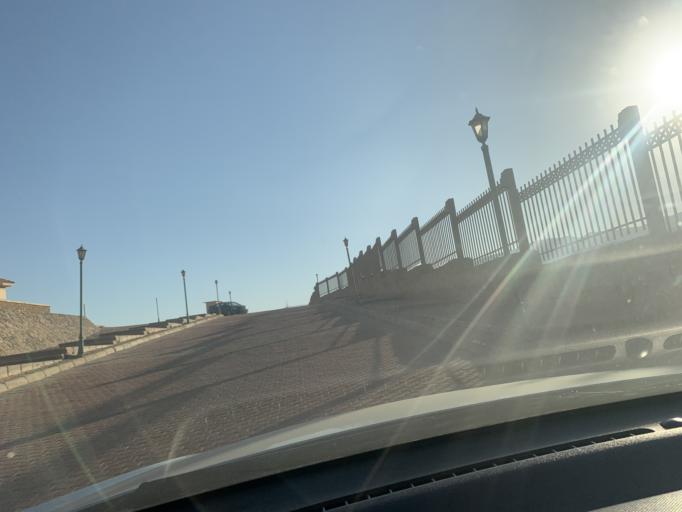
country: EG
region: As Suways
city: Ain Sukhna
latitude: 29.3748
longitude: 32.5690
